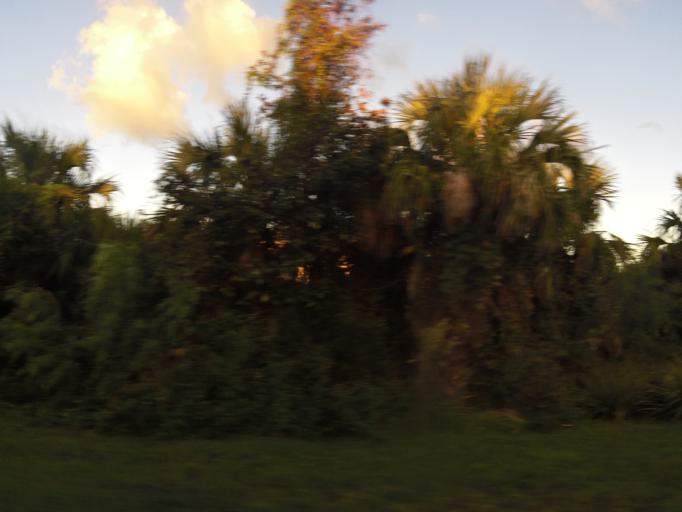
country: US
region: Florida
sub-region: Saint Johns County
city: Sawgrass
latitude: 30.1934
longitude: -81.3666
